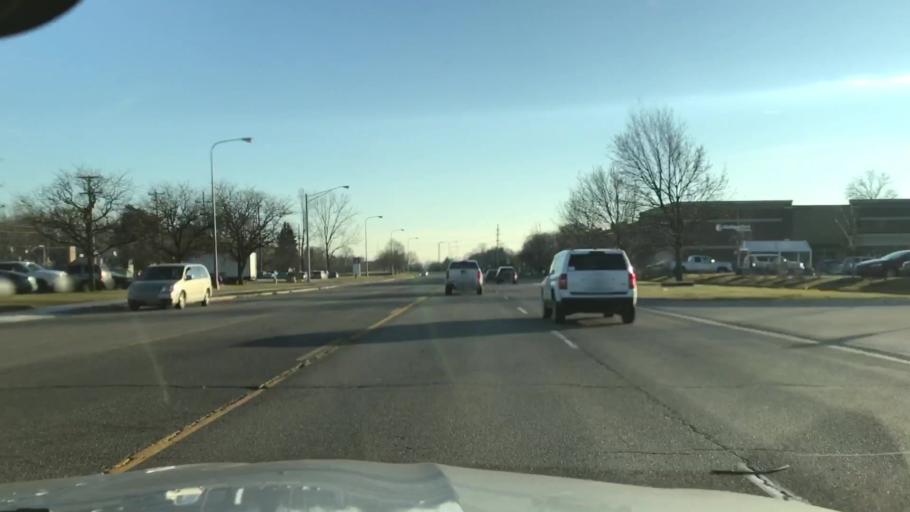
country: US
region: Michigan
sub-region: Oakland County
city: Madison Heights
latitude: 42.5030
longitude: -83.1181
